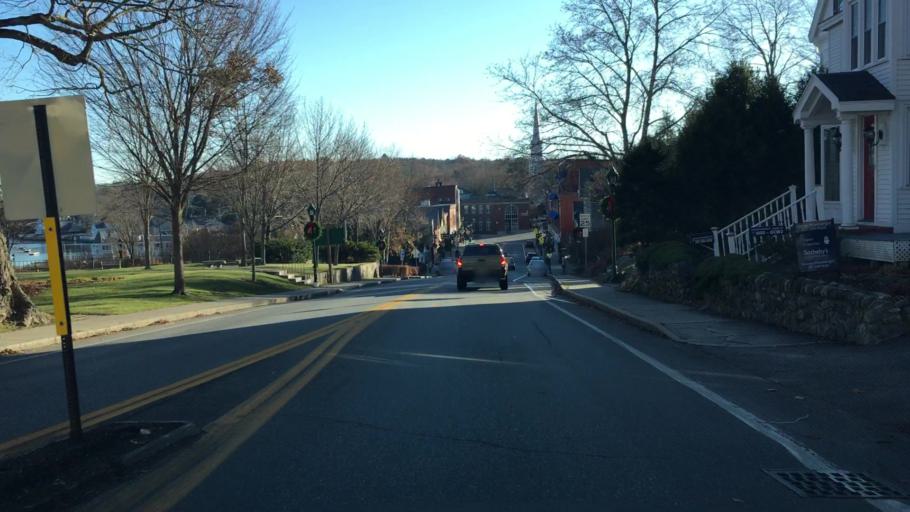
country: US
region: Maine
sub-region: Knox County
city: Camden
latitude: 44.2118
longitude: -69.0649
